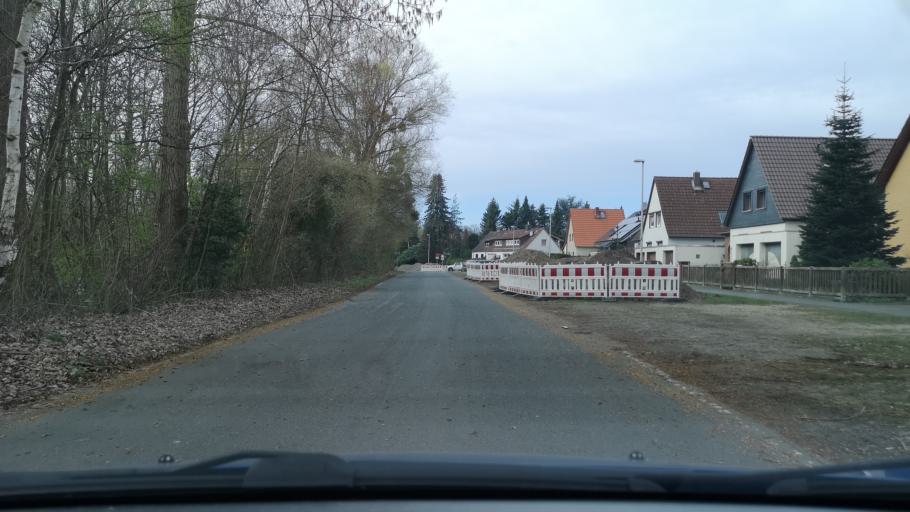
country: DE
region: Lower Saxony
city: Hannover
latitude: 52.4096
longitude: 9.6810
